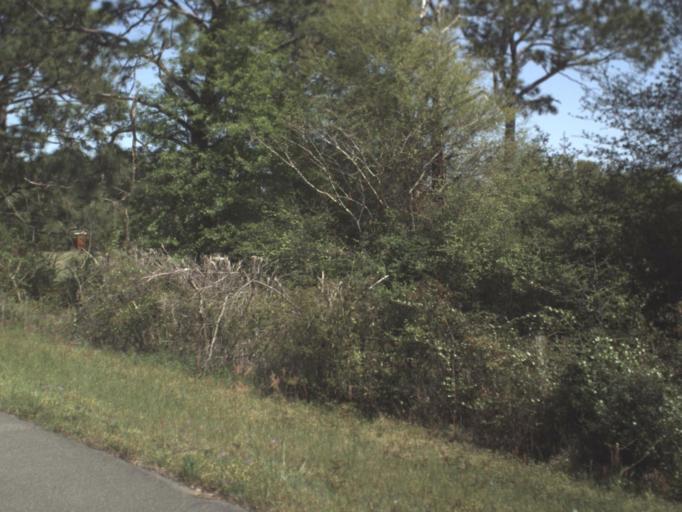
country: US
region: Florida
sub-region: Okaloosa County
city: Crestview
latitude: 30.7076
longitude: -86.7695
